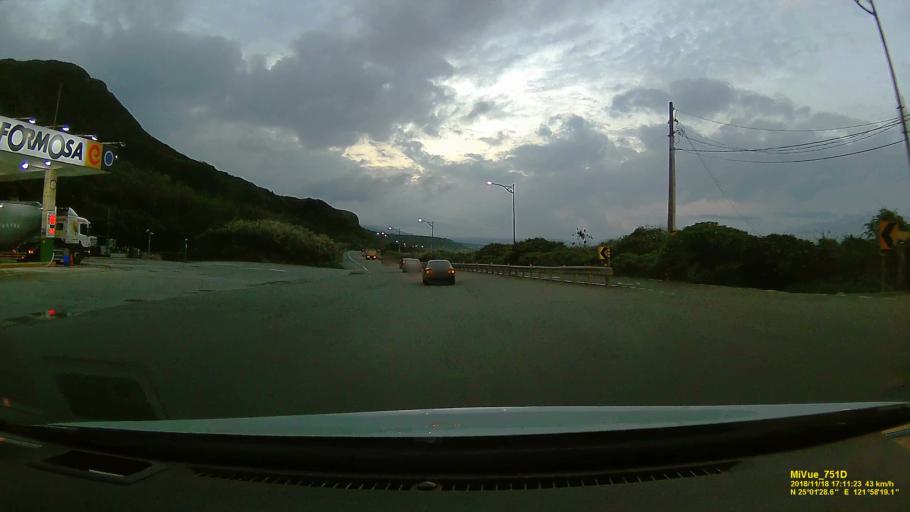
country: TW
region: Taiwan
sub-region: Keelung
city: Keelung
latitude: 25.0246
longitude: 121.9718
